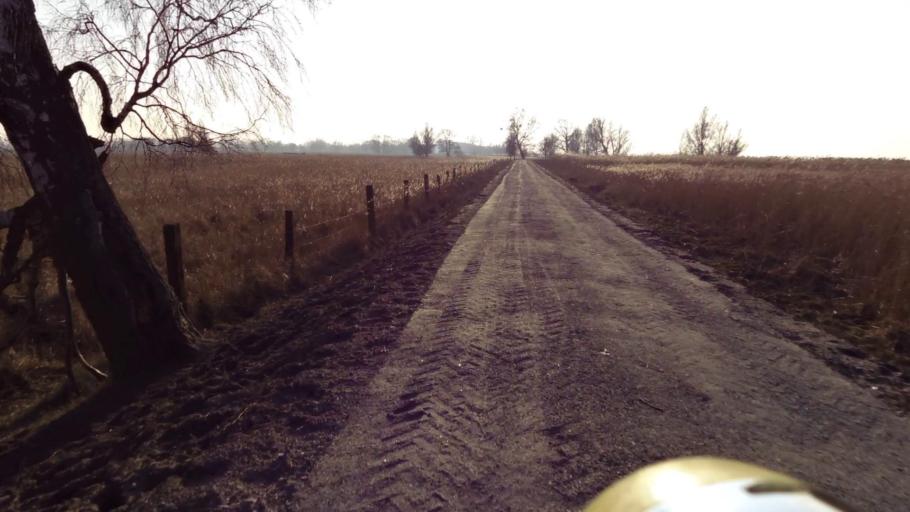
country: PL
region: West Pomeranian Voivodeship
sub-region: Powiat goleniowski
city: Stepnica
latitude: 53.7378
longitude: 14.5555
